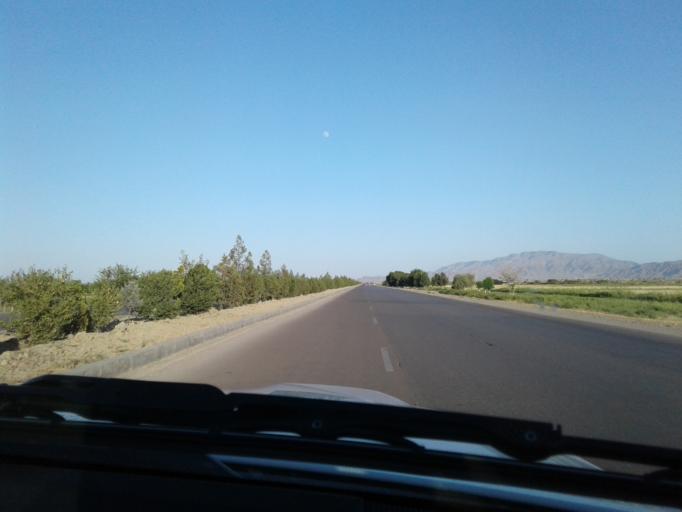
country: TM
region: Ahal
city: Baharly
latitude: 38.3423
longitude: 57.5613
